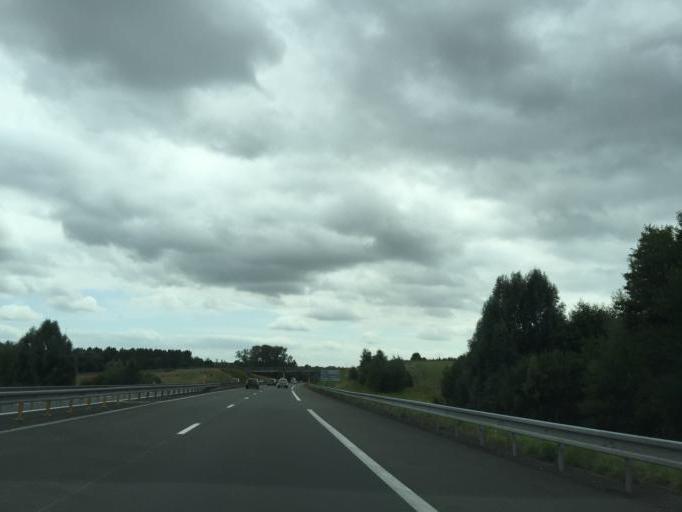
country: FR
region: Pays de la Loire
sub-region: Departement de la Sarthe
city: Marigne-Laille
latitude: 47.8126
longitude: 0.3072
